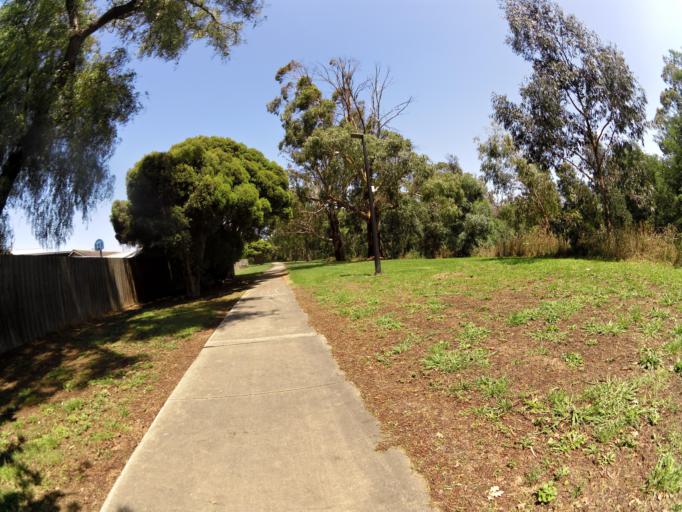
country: AU
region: Victoria
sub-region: Latrobe
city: Traralgon
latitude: -38.1988
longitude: 146.5421
